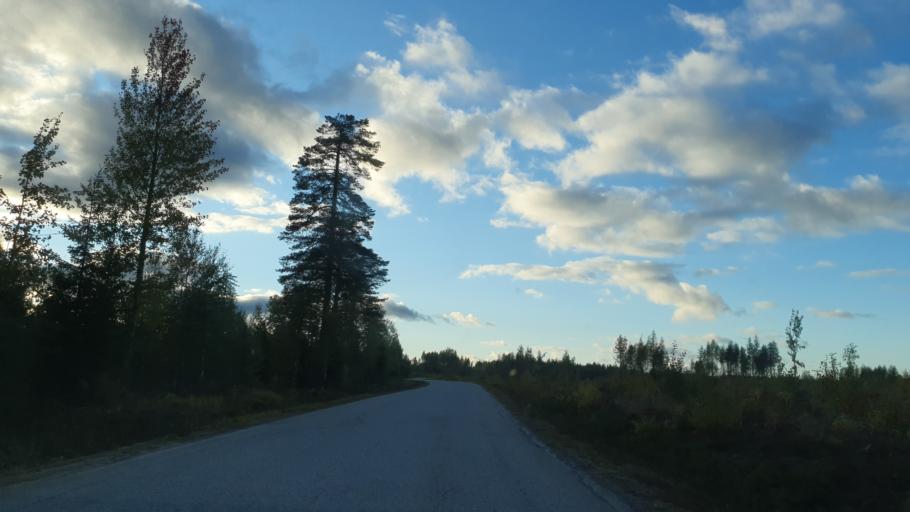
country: FI
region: Kainuu
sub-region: Kehys-Kainuu
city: Kuhmo
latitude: 63.9481
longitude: 29.7613
